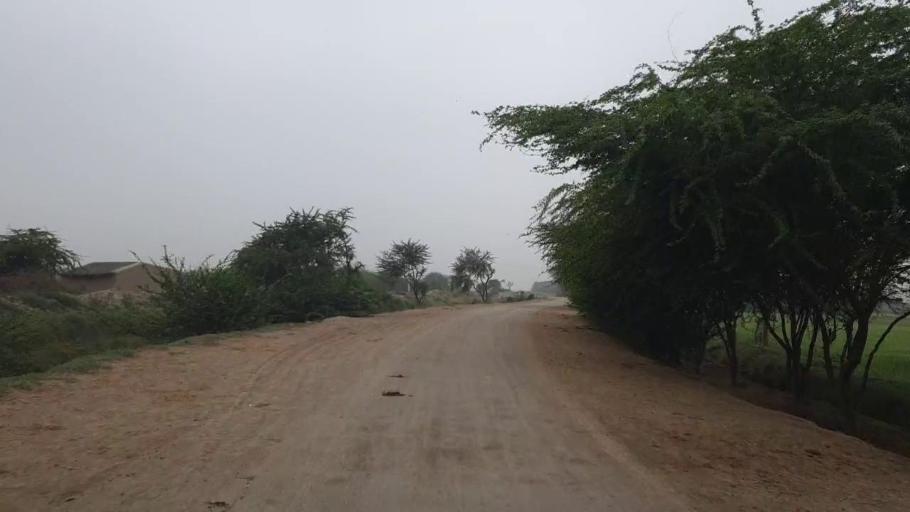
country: PK
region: Sindh
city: Badin
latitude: 24.6000
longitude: 68.6747
